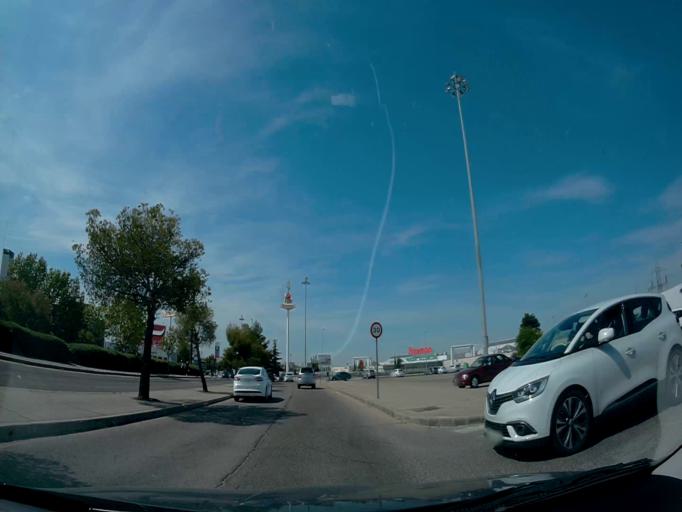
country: ES
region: Madrid
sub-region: Provincia de Madrid
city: Alcorcon
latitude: 40.3476
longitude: -3.8519
